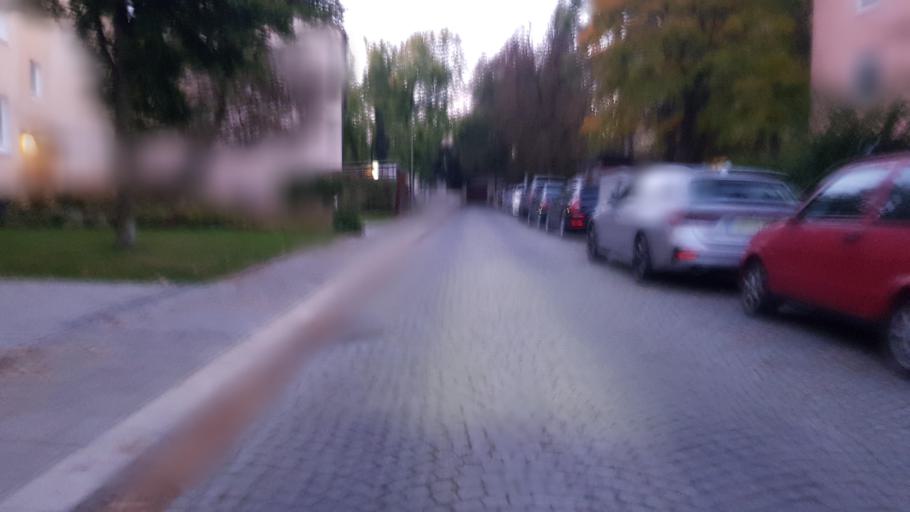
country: DE
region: Bavaria
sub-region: Upper Bavaria
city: Karlsfeld
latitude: 48.1767
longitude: 11.5079
